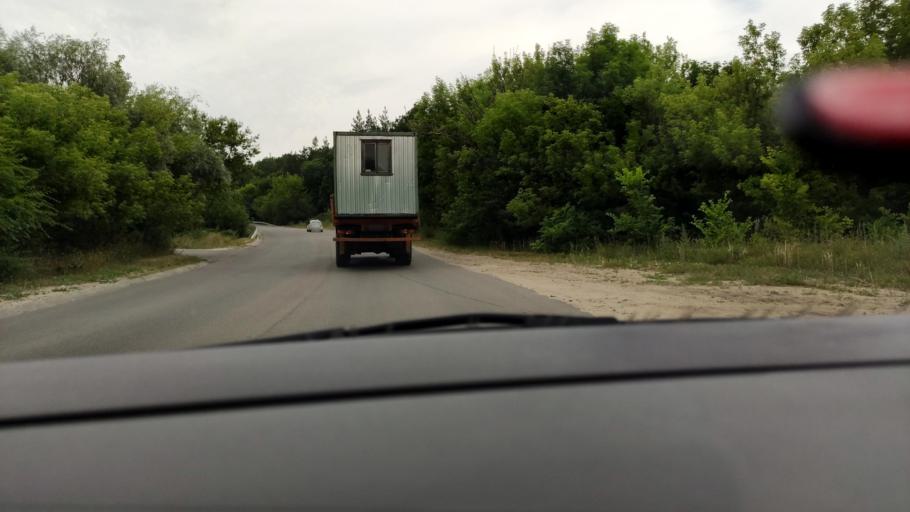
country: RU
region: Voronezj
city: Ramon'
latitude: 51.9036
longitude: 39.3407
